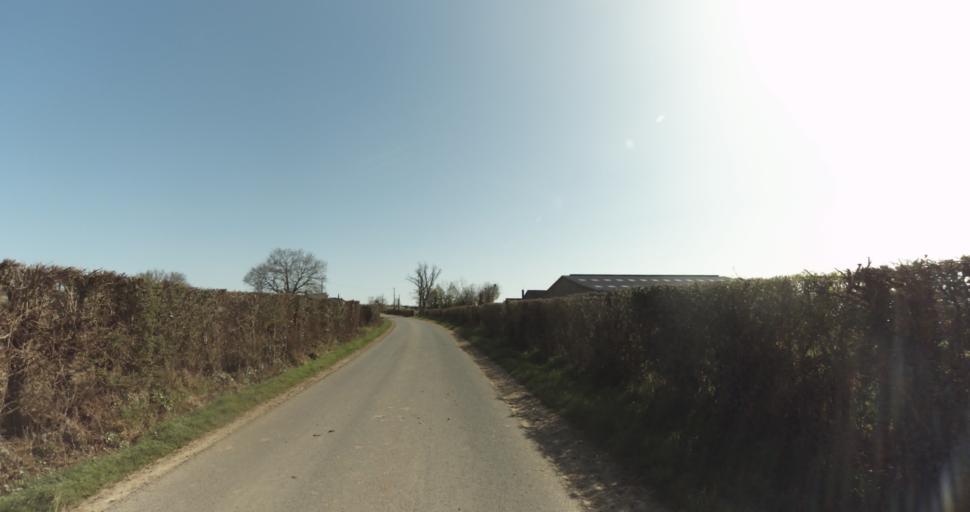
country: FR
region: Lower Normandy
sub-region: Departement de l'Orne
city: Trun
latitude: 48.9218
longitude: 0.0286
